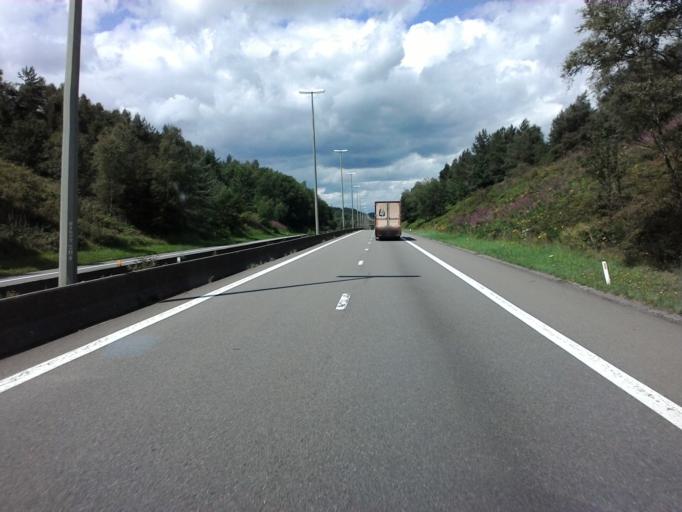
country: BE
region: Wallonia
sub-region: Province du Luxembourg
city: Manhay
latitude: 50.3371
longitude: 5.6955
